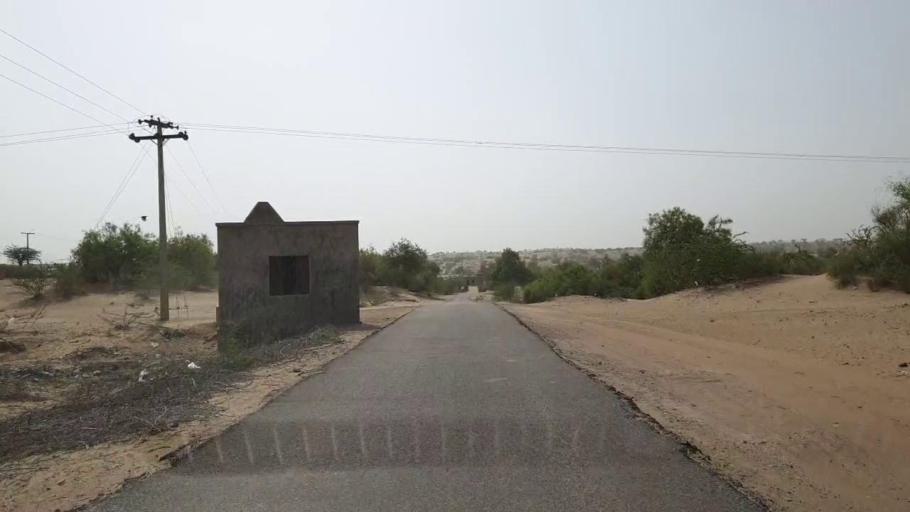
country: PK
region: Sindh
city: Mithi
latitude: 24.5767
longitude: 69.9275
